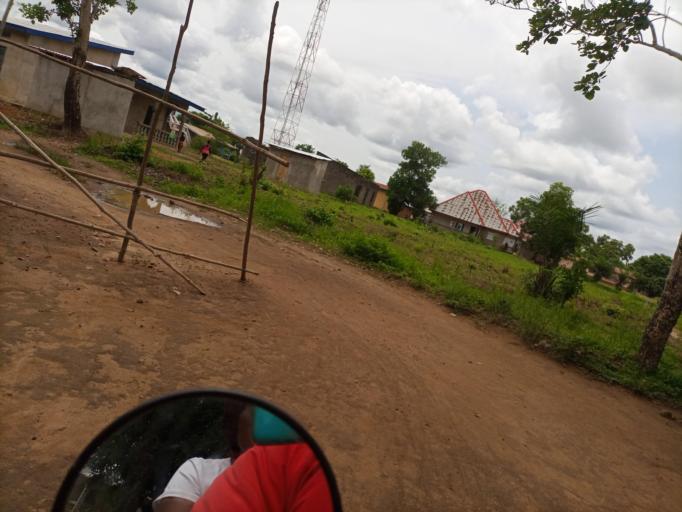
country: SL
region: Southern Province
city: Bo
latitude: 7.9644
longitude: -11.7161
